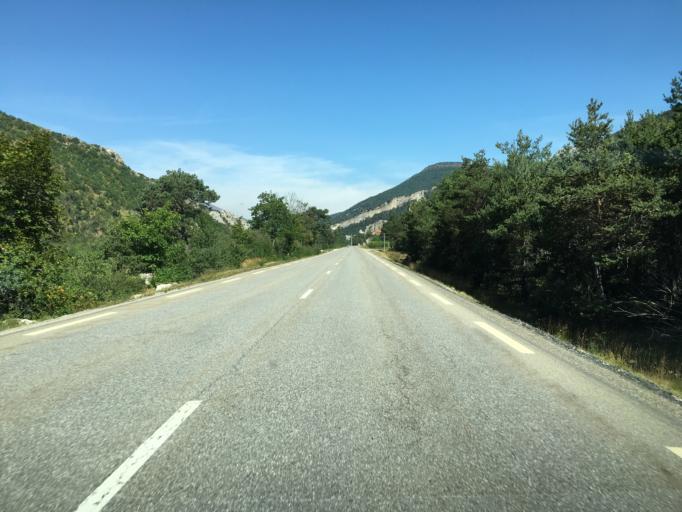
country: FR
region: Provence-Alpes-Cote d'Azur
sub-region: Departement des Hautes-Alpes
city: Veynes
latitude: 44.5822
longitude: 5.7232
